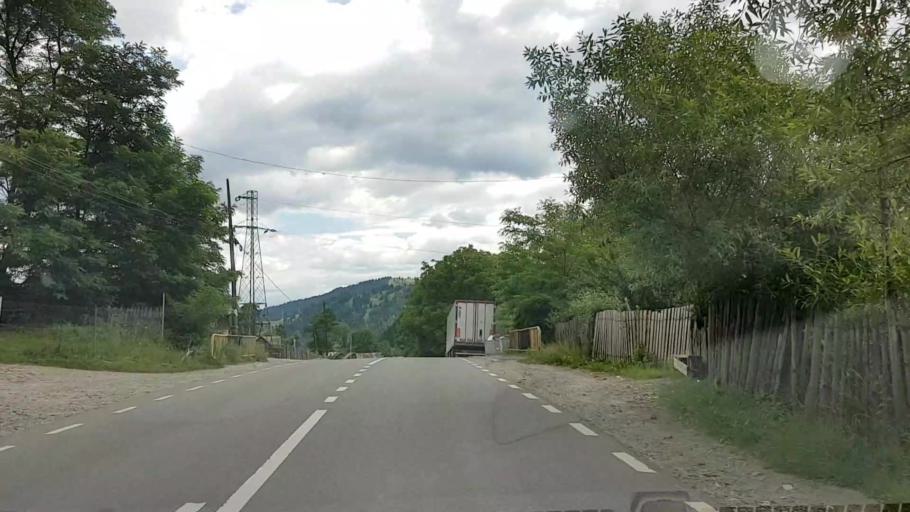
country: RO
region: Neamt
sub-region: Comuna Farcasa
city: Farcasa
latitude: 47.1675
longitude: 25.8045
